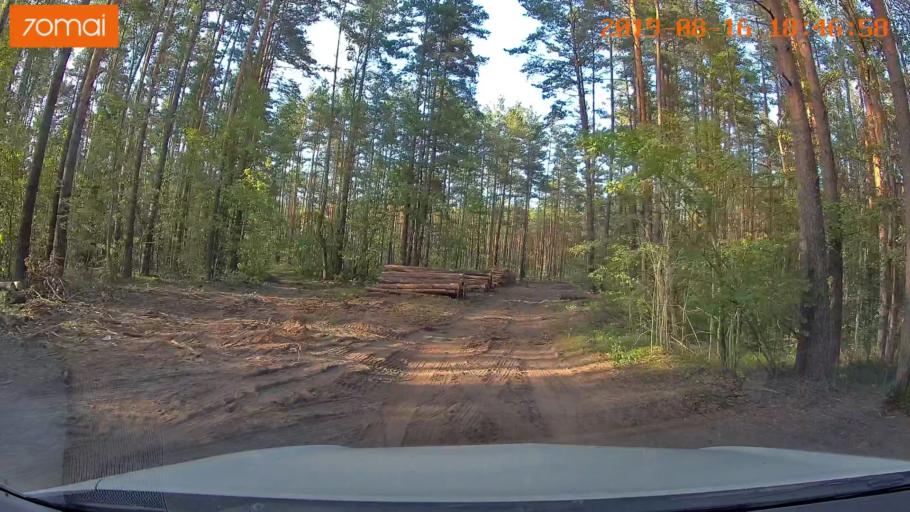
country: BY
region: Mogilev
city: Asipovichy
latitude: 53.2296
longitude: 28.6650
